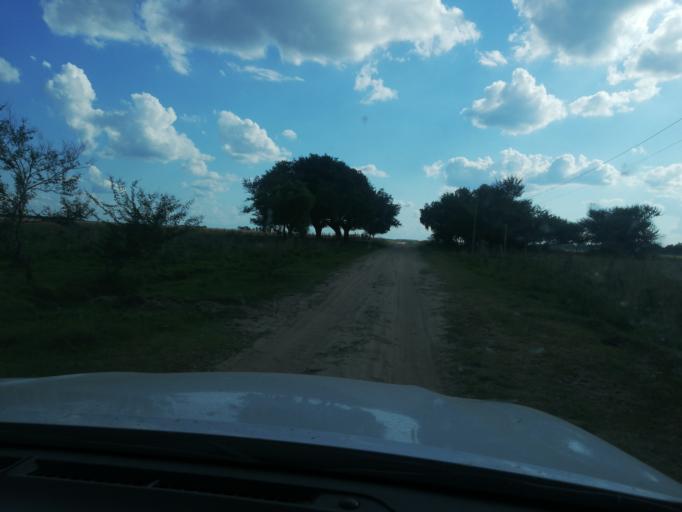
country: AR
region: Corrientes
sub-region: Departamento de San Miguel
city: San Miguel
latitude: -27.9917
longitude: -57.5705
